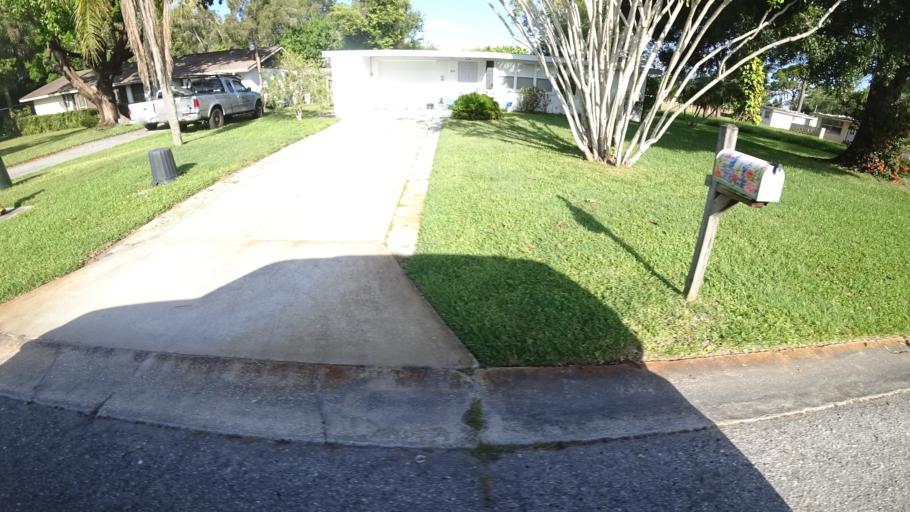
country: US
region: Florida
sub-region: Manatee County
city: West Samoset
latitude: 27.4467
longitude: -82.5570
